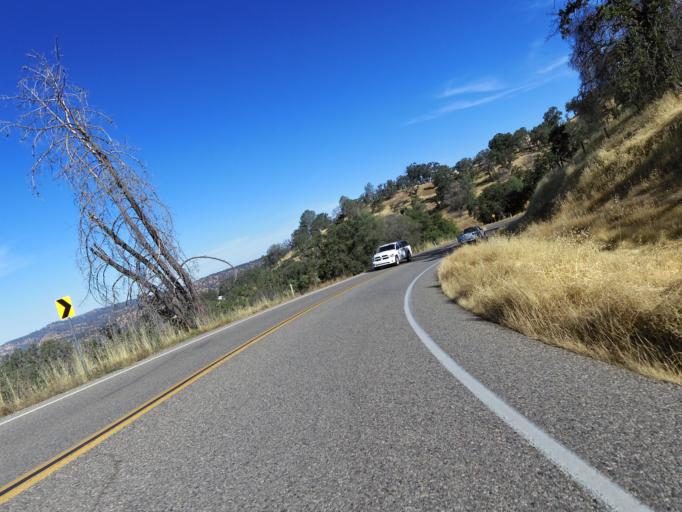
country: US
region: California
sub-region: Madera County
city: Yosemite Lakes
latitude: 37.2282
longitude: -119.7553
